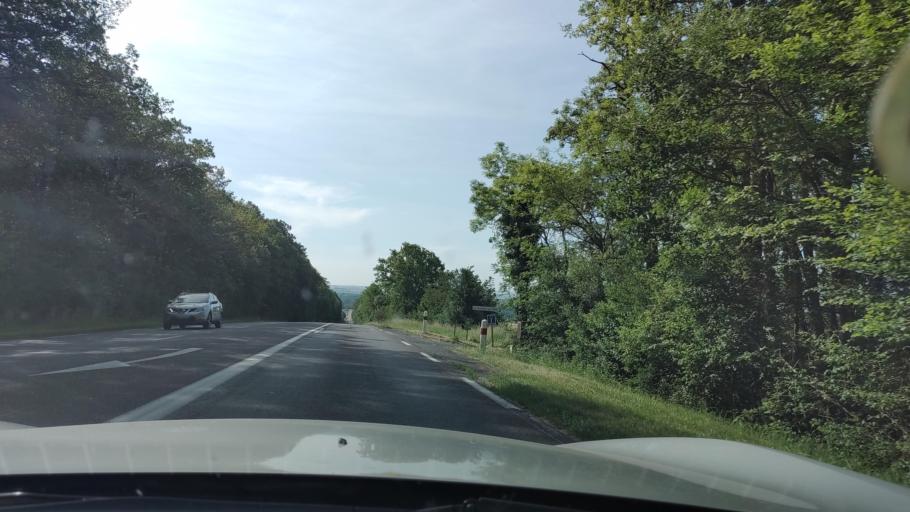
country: FR
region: Ile-de-France
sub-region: Departement de Seine-et-Marne
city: Sourdun
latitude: 48.5269
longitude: 3.4067
